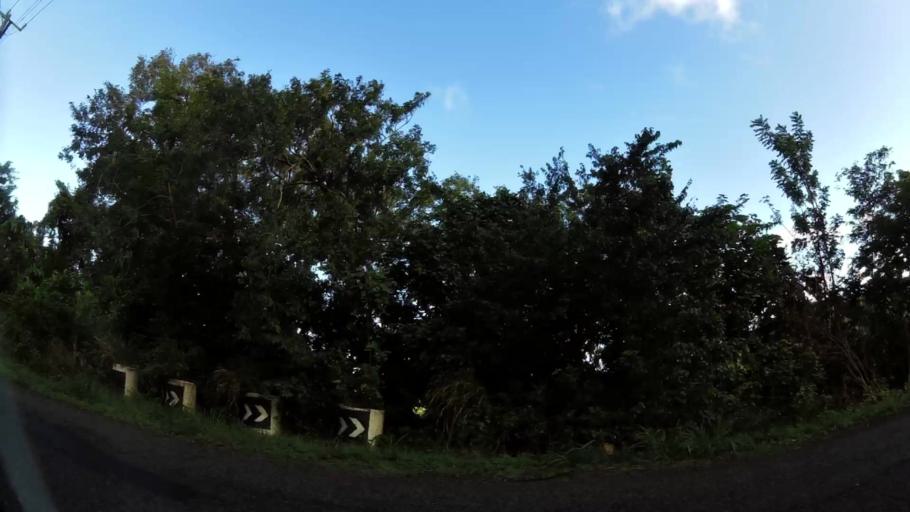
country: LC
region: Anse-la-Raye
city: Canaries
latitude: 13.9180
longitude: -61.0423
